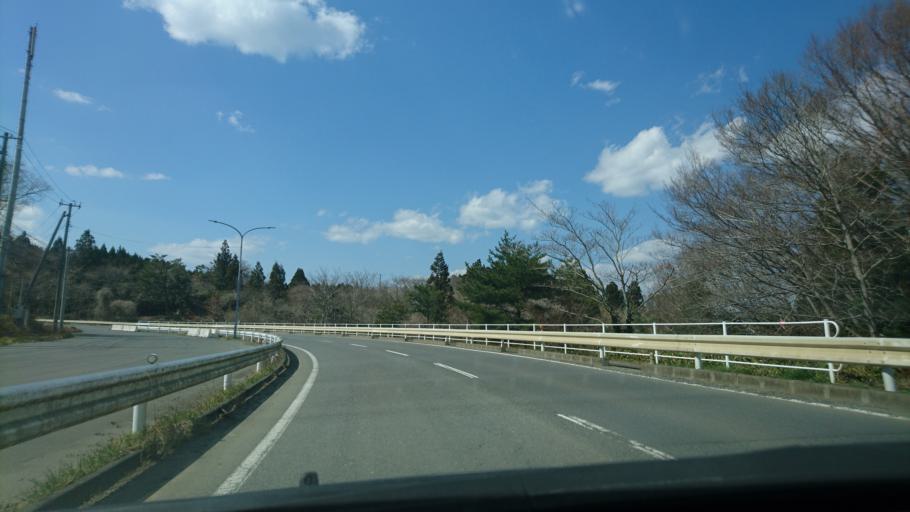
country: JP
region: Miyagi
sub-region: Oshika Gun
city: Onagawa Cho
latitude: 38.6391
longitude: 141.4986
